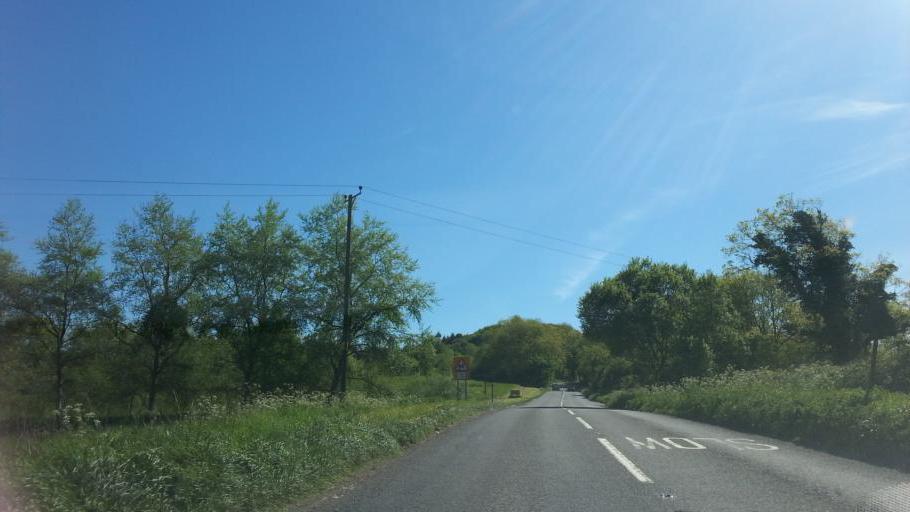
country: GB
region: England
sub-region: Dorset
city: Shaftesbury
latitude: 51.0359
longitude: -2.1852
